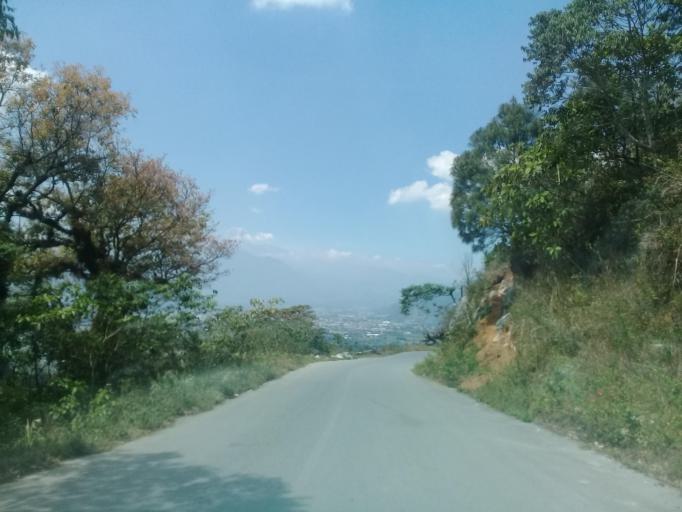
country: MX
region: Veracruz
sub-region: Tlilapan
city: Tonalixco
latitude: 18.8015
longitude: -97.0585
